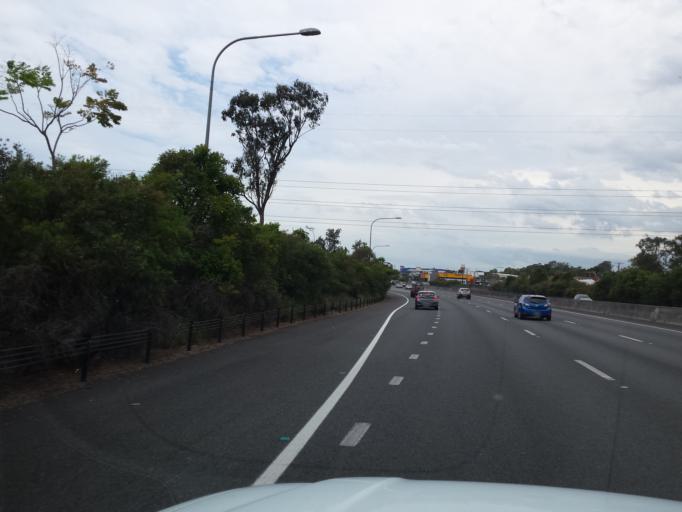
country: AU
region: Queensland
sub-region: Gold Coast
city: Nerang
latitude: -28.0038
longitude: 153.3403
